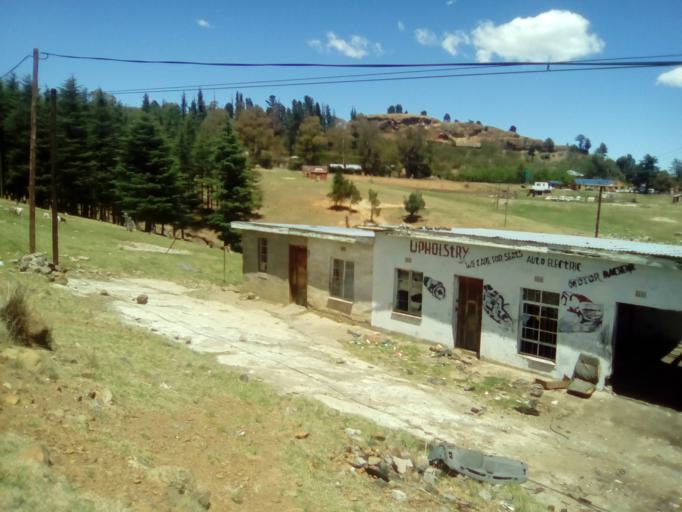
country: LS
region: Qacha's Nek
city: Qacha's Nek
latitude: -30.1192
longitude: 28.6916
